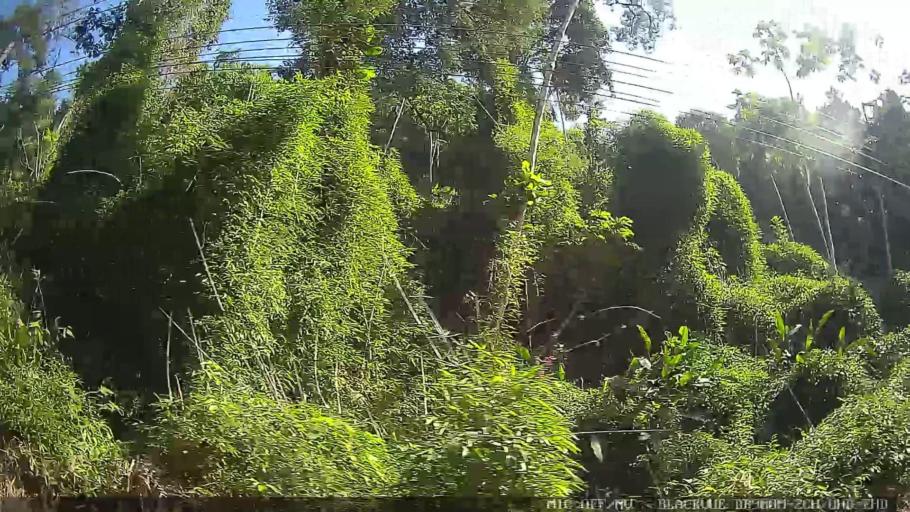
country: BR
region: Sao Paulo
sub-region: Santos
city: Santos
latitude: -23.9994
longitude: -46.3118
